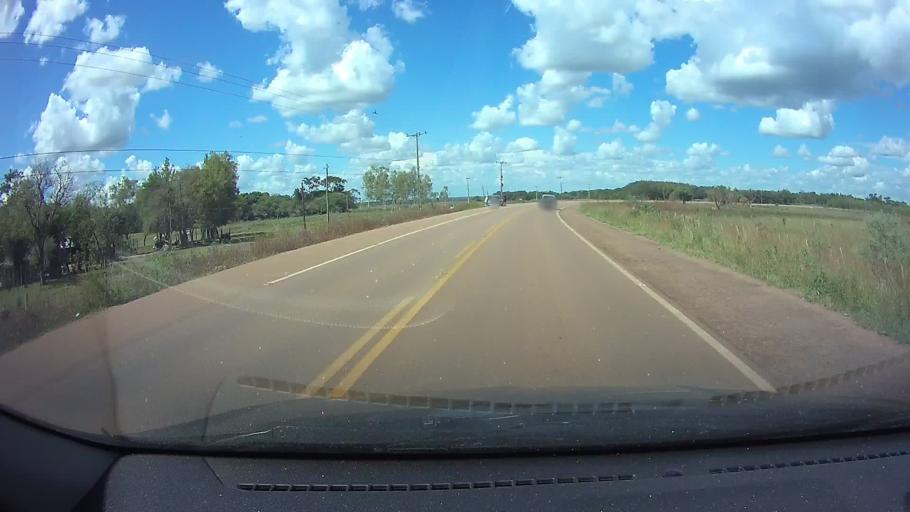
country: PY
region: Paraguari
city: La Colmena
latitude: -25.9147
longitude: -56.7159
